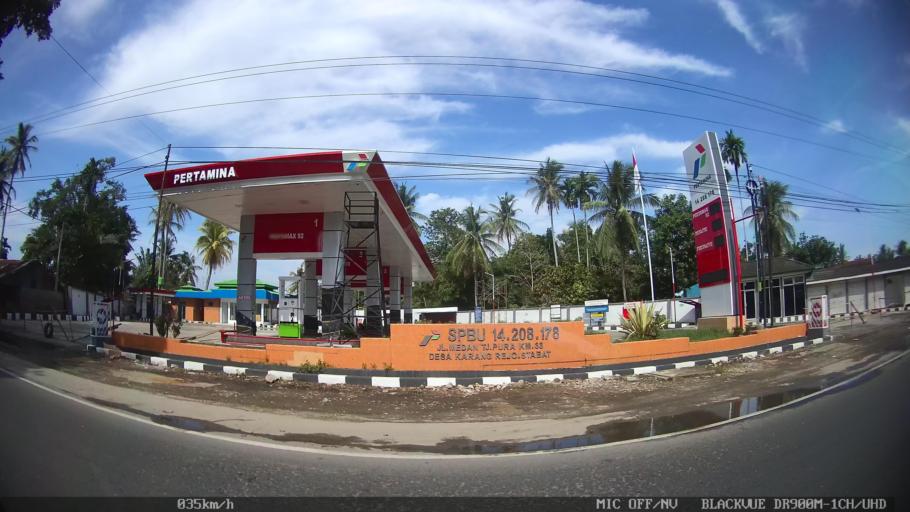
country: ID
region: North Sumatra
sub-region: Kabupaten Langkat
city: Stabat
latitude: 3.7080
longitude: 98.5060
